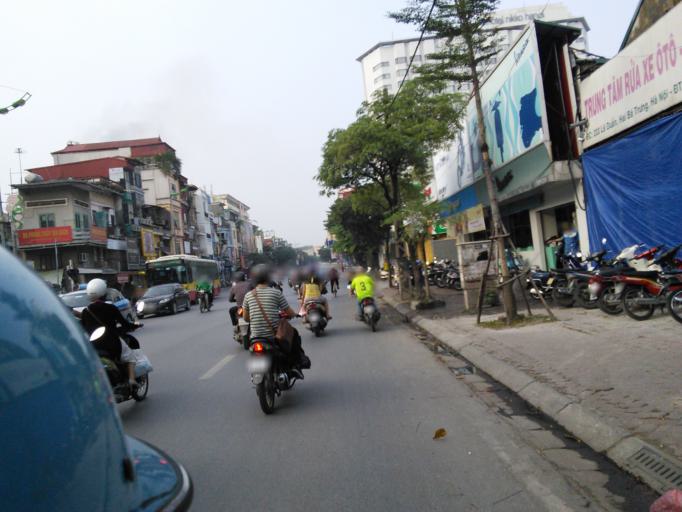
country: VN
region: Ha Noi
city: Hai BaTrung
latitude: 21.0164
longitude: 105.8414
